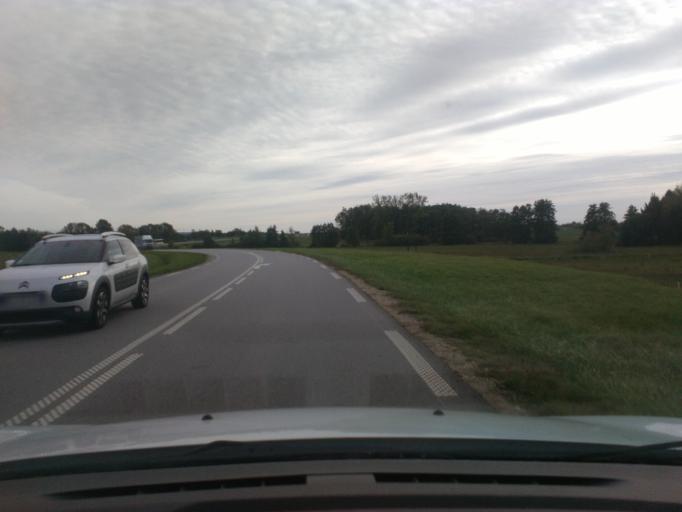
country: FR
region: Lorraine
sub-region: Departement des Vosges
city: Rambervillers
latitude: 48.3207
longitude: 6.6296
